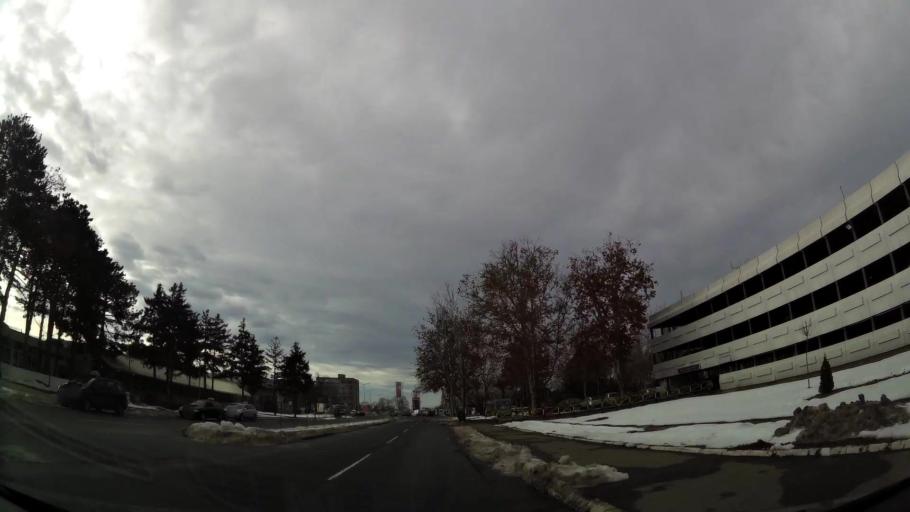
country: RS
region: Central Serbia
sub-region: Belgrade
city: Surcin
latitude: 44.8184
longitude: 20.2893
